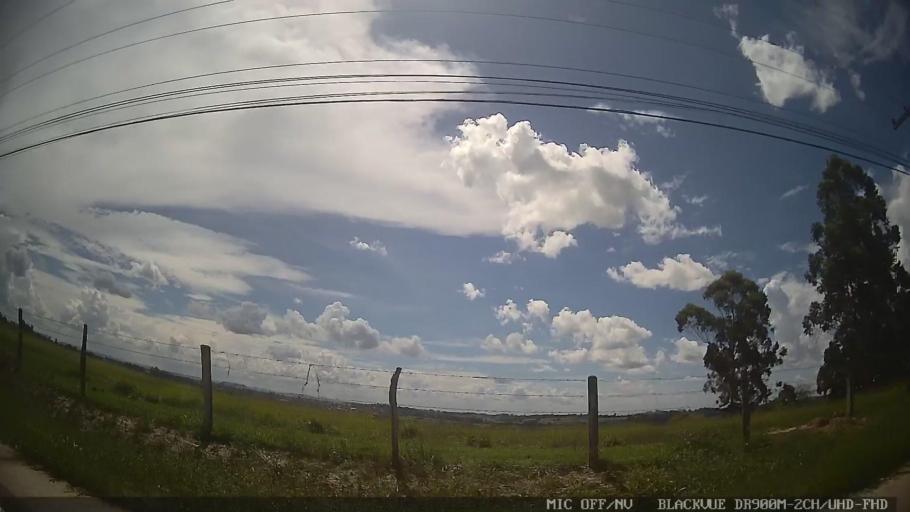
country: BR
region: Sao Paulo
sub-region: Conchas
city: Conchas
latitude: -23.0354
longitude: -48.0168
